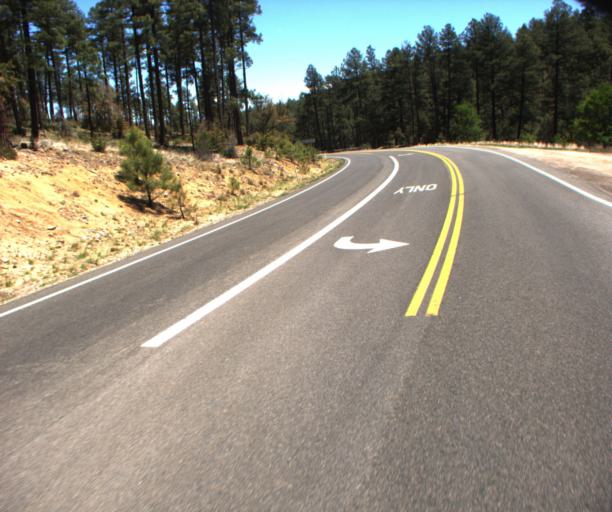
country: US
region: Arizona
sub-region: Yavapai County
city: Prescott
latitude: 34.4959
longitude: -112.4861
